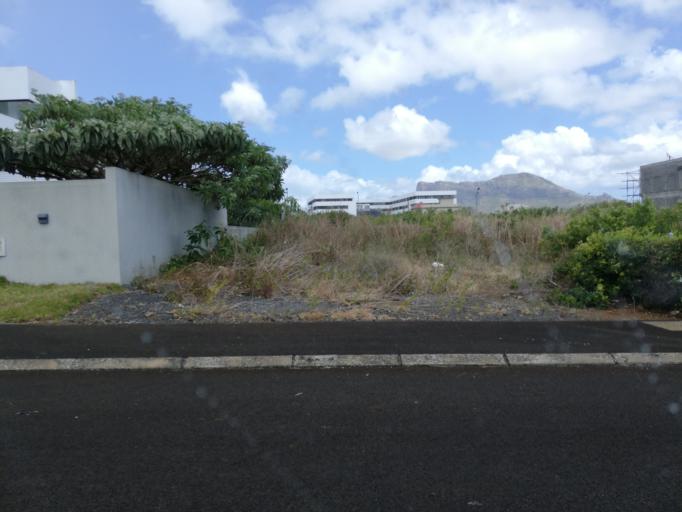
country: MU
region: Plaines Wilhems
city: Ebene
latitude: -20.2383
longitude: 57.4865
